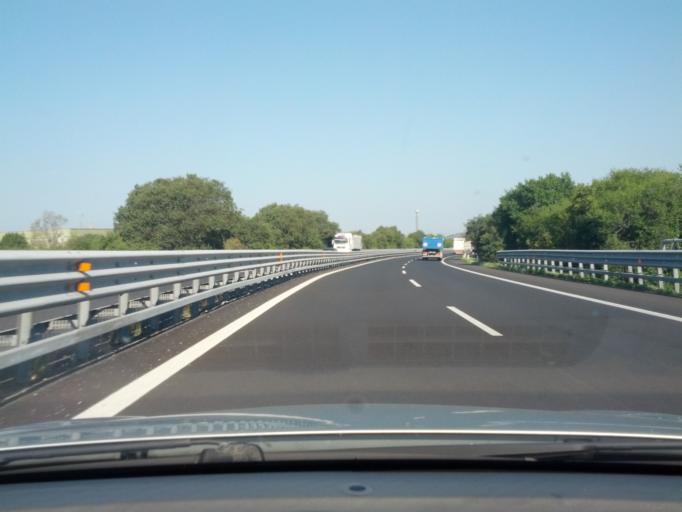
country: IT
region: Friuli Venezia Giulia
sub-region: Provincia di Trieste
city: Duino
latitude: 45.7784
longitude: 13.6027
